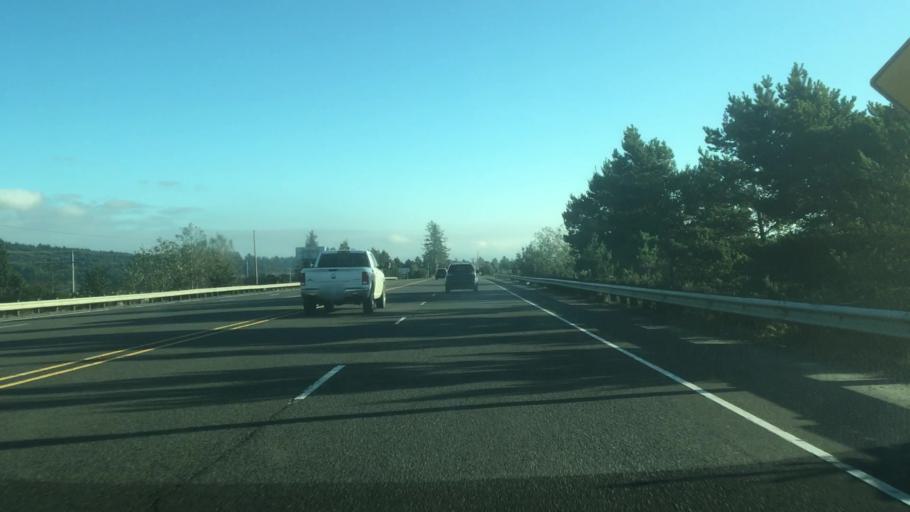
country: US
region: Oregon
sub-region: Clatsop County
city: Warrenton
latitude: 46.1224
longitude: -123.9264
